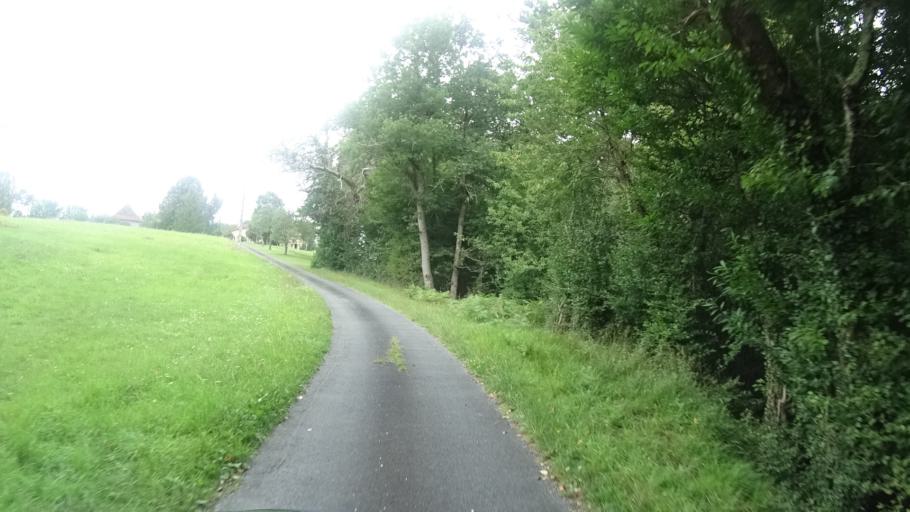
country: FR
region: Aquitaine
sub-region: Departement de la Dordogne
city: Lembras
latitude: 44.9779
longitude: 0.4753
